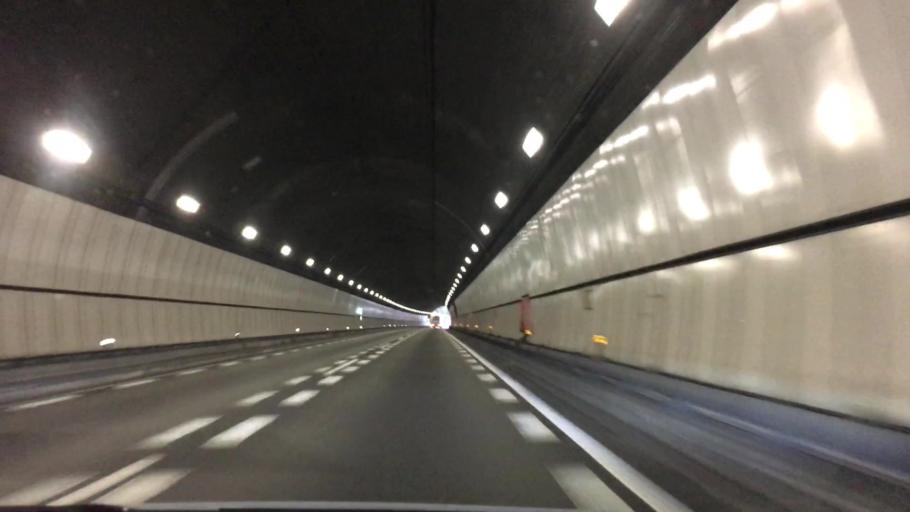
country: JP
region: Shizuoka
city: Fuji
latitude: 35.1237
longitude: 138.6082
